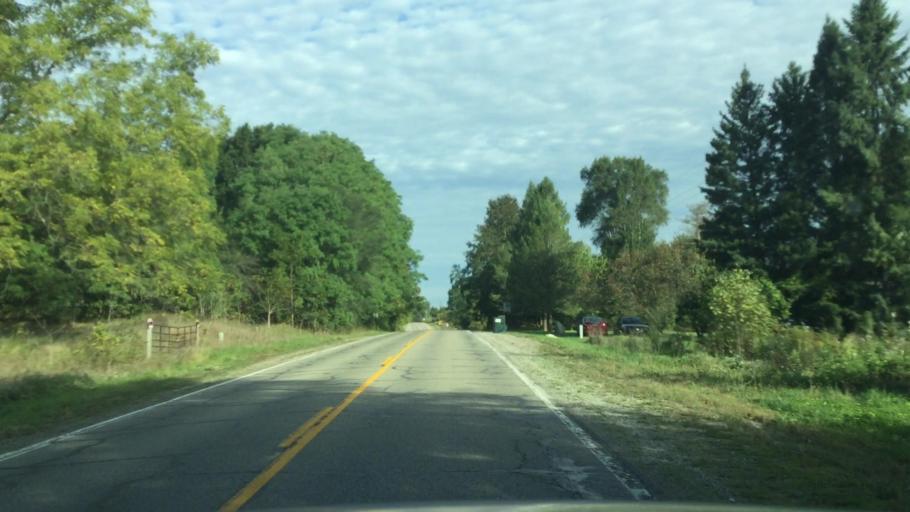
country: US
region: Michigan
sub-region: Livingston County
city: Howell
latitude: 42.5511
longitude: -83.8822
